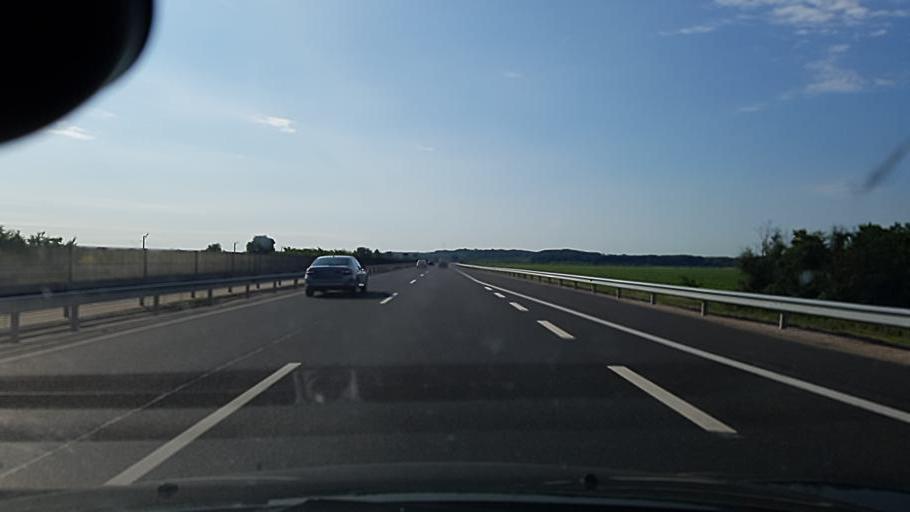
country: HU
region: Fejer
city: Adony
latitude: 47.0889
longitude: 18.8594
